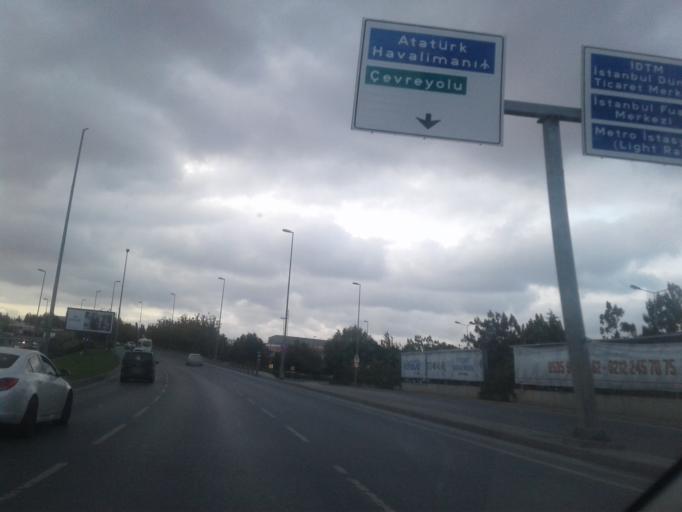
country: TR
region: Istanbul
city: Bahcelievler
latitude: 40.9852
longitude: 28.8295
